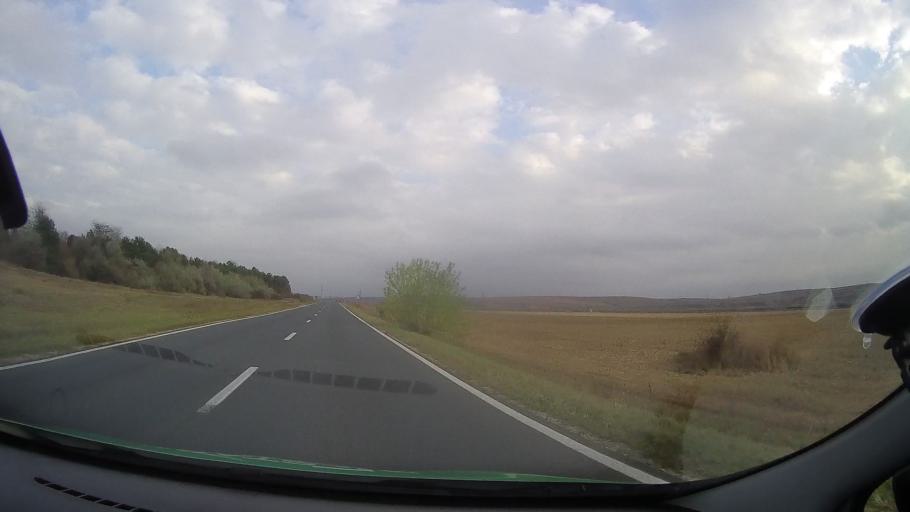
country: RO
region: Constanta
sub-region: Comuna Mircea Voda
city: Mircea Voda
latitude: 44.2690
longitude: 28.1781
